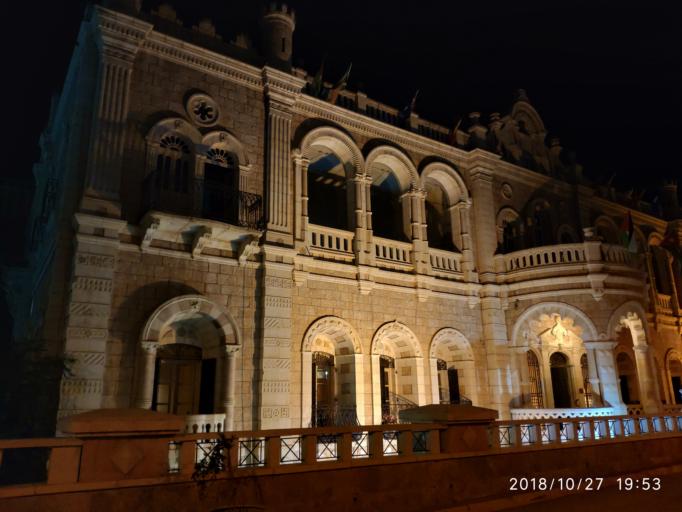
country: PS
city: Khallat Hamamah
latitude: 31.7171
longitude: 35.2014
